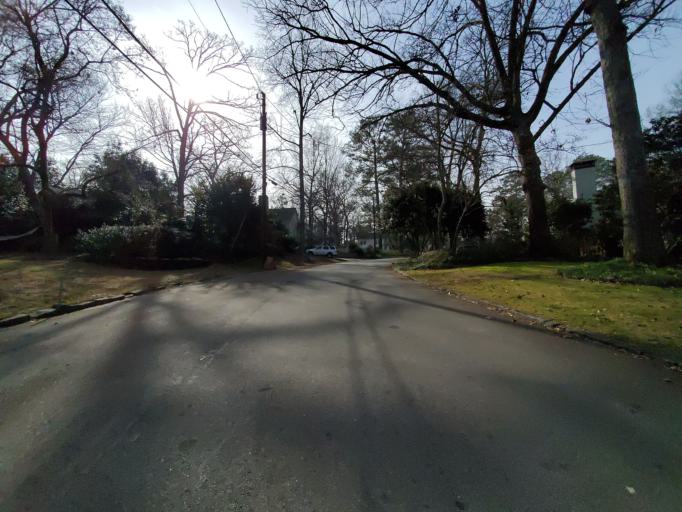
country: US
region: Georgia
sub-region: DeKalb County
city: North Decatur
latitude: 33.7797
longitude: -84.3104
